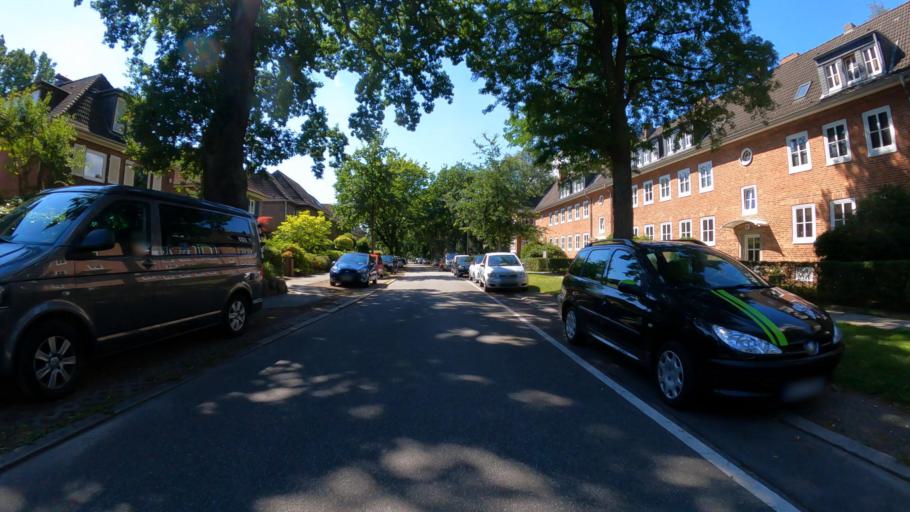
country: DE
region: Hamburg
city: Alsterdorf
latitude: 53.6105
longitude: 10.0158
